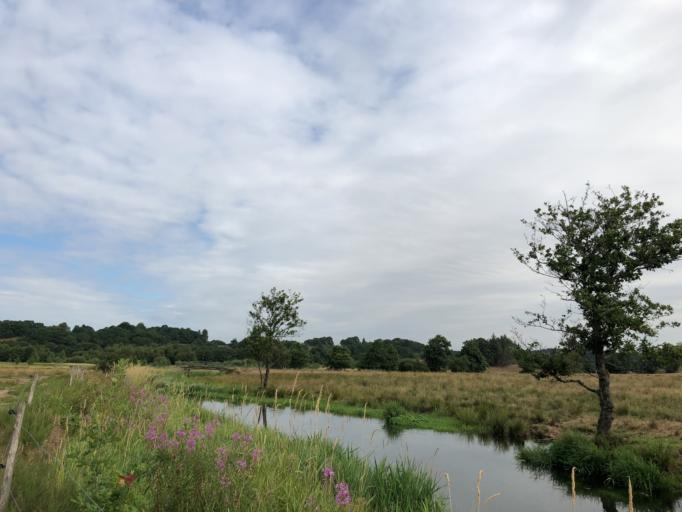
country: DK
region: South Denmark
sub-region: Vejle Kommune
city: Egtved
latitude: 55.6498
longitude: 9.2799
